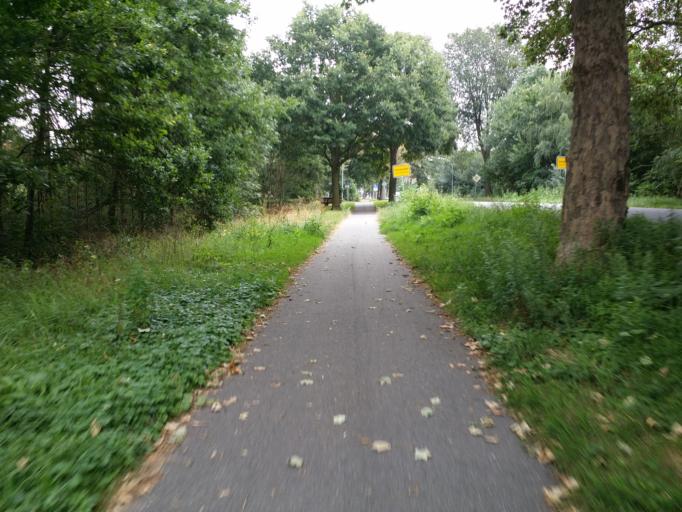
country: DE
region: Schleswig-Holstein
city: Krempermoor
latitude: 53.8785
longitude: 9.4751
